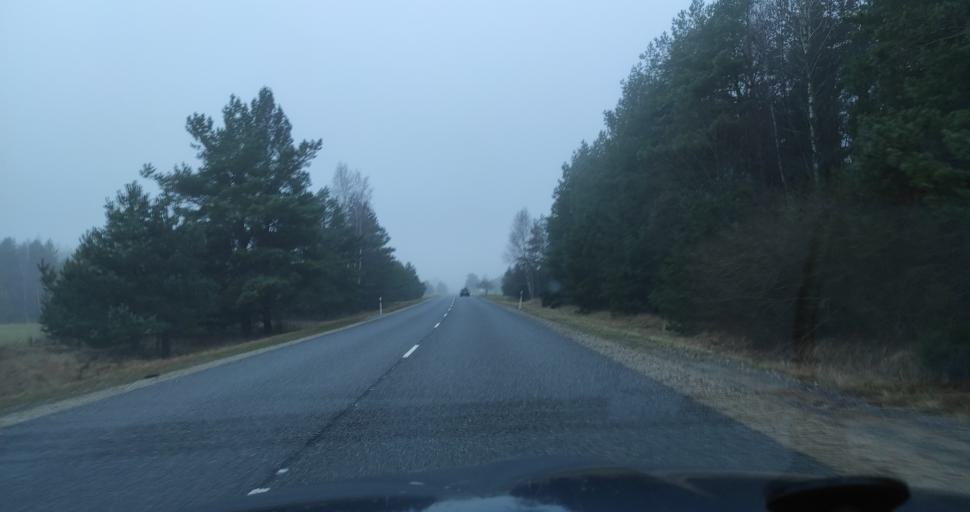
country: LV
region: Pavilostas
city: Pavilosta
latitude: 56.9584
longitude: 21.3241
